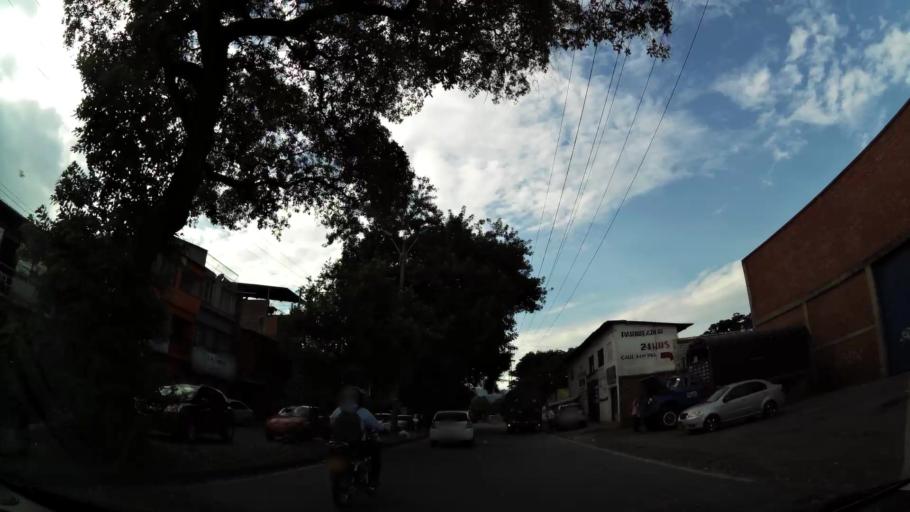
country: CO
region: Valle del Cauca
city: Cali
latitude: 3.4557
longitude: -76.5124
